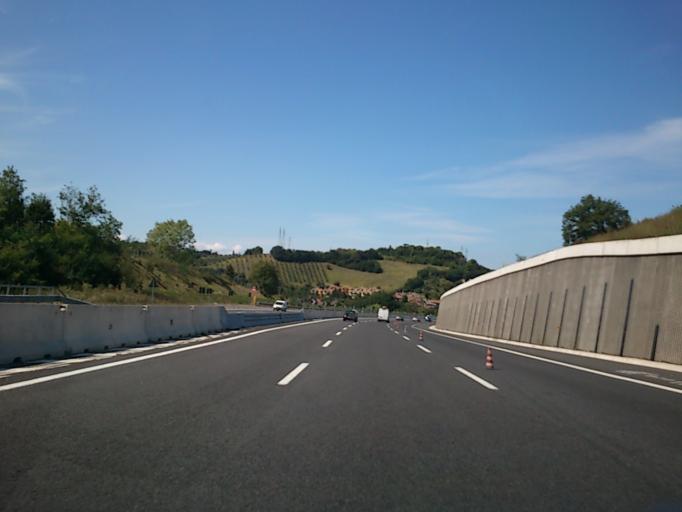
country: IT
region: The Marches
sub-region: Provincia di Pesaro e Urbino
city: Pesaro
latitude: 43.8796
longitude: 12.9098
